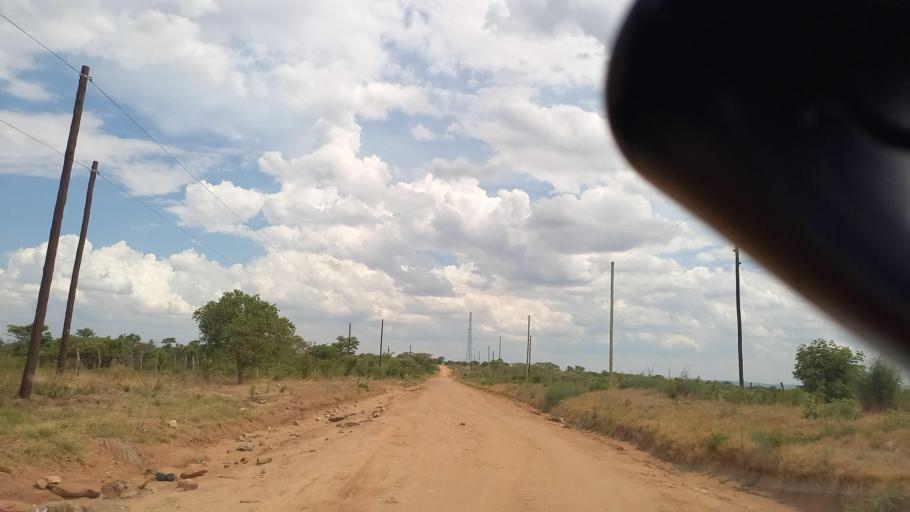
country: ZM
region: Southern
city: Nakambala
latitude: -16.0294
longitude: 27.9681
